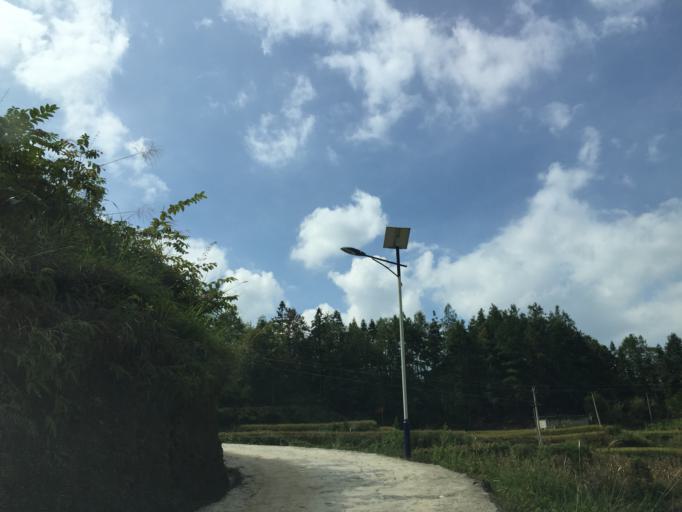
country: CN
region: Guizhou Sheng
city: Quankou
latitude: 28.5355
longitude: 108.1182
